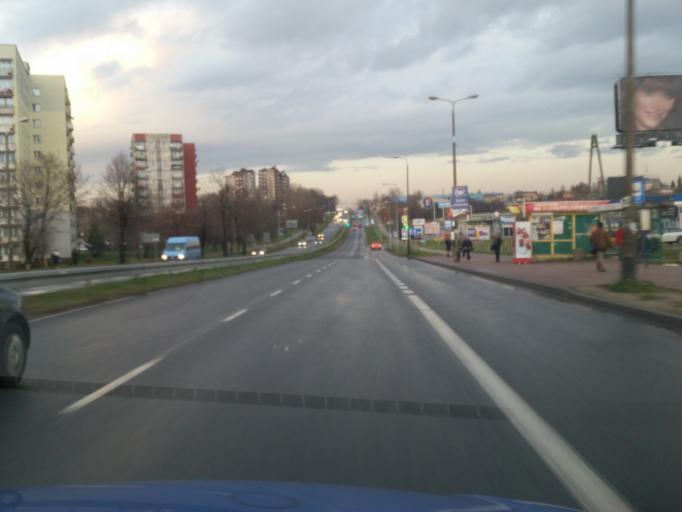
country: PL
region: Silesian Voivodeship
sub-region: Dabrowa Gornicza
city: Dabrowa Gornicza
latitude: 50.2906
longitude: 19.1811
